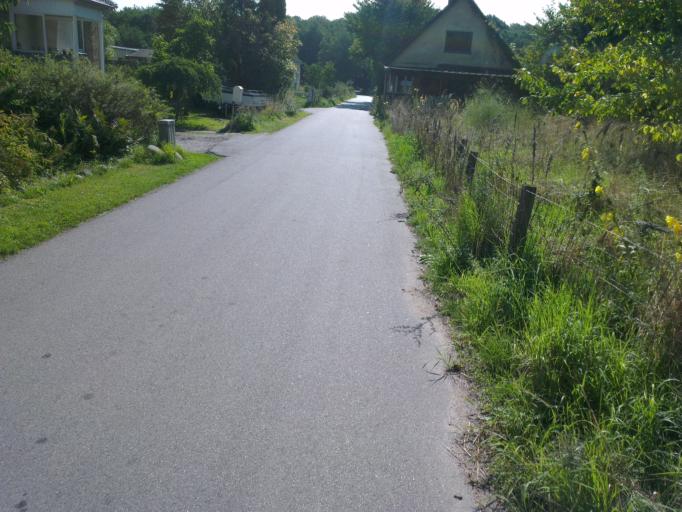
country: DK
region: Capital Region
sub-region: Frederikssund Kommune
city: Frederikssund
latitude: 55.8346
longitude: 12.0324
